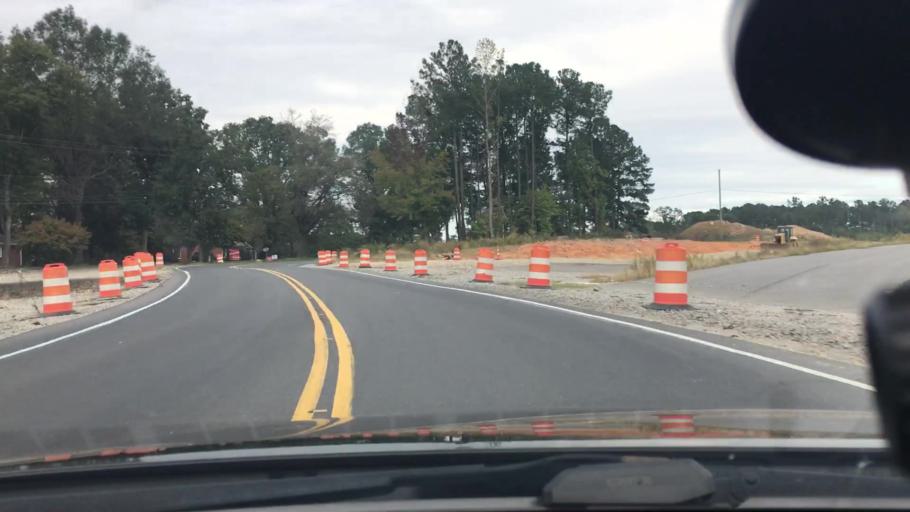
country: US
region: North Carolina
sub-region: Montgomery County
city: Troy
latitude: 35.3401
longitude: -79.9204
